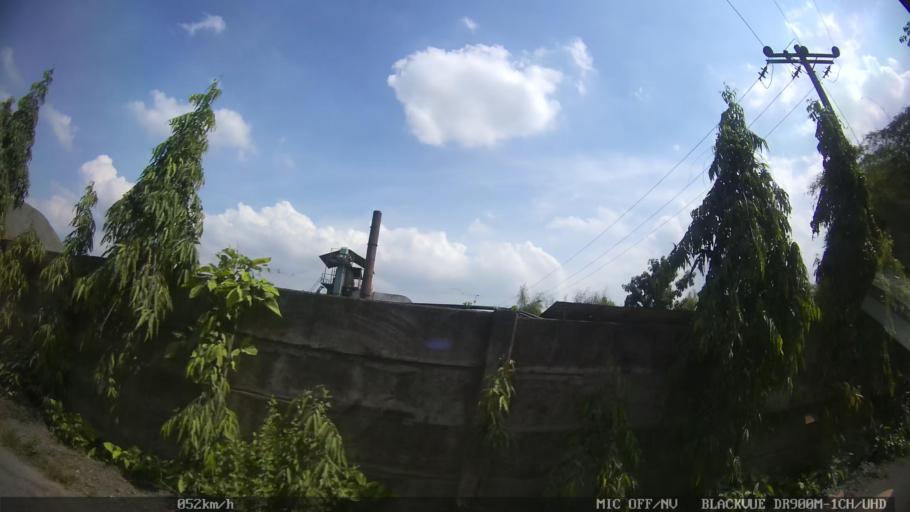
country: ID
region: North Sumatra
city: Binjai
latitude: 3.6354
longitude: 98.5343
